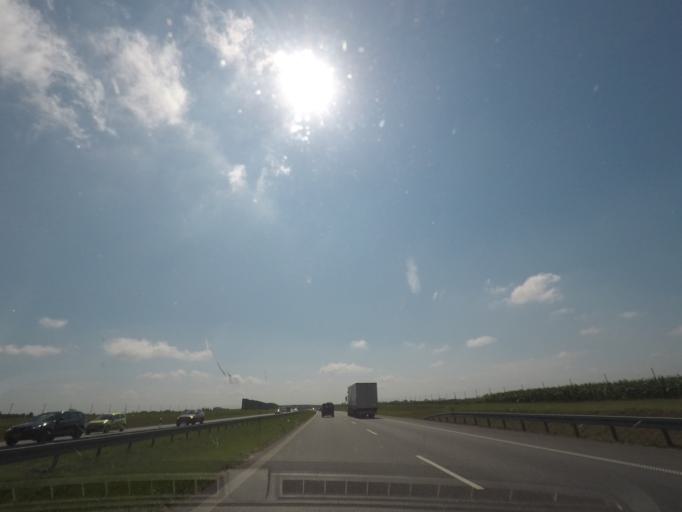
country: PL
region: Kujawsko-Pomorskie
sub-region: Powiat wloclawski
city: Czerniewice
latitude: 52.5392
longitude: 19.0575
